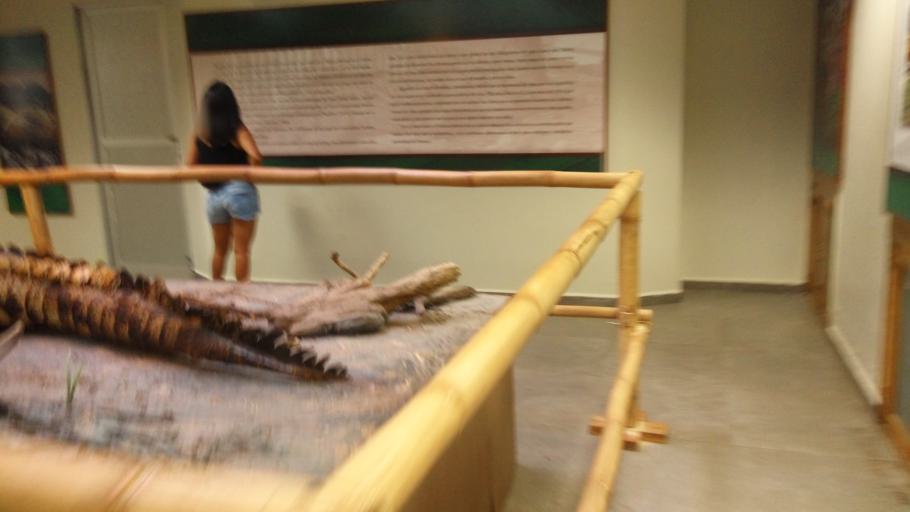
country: MX
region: Tabasco
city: Villahermosa
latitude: 17.9997
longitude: -92.9370
